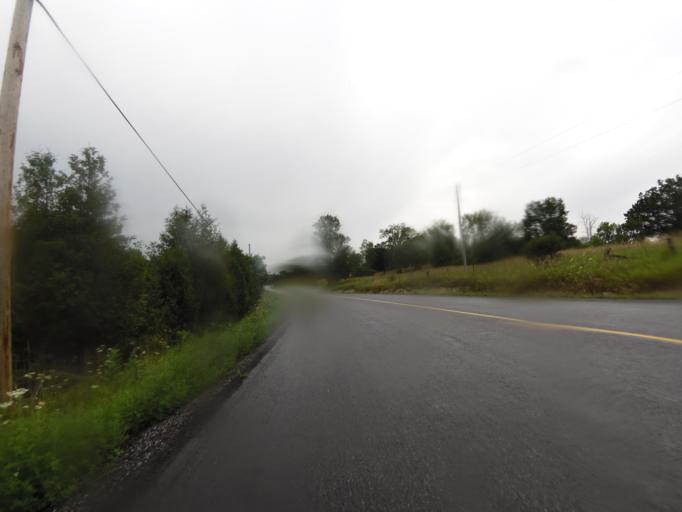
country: CA
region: Ontario
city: Perth
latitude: 44.9394
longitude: -76.4380
